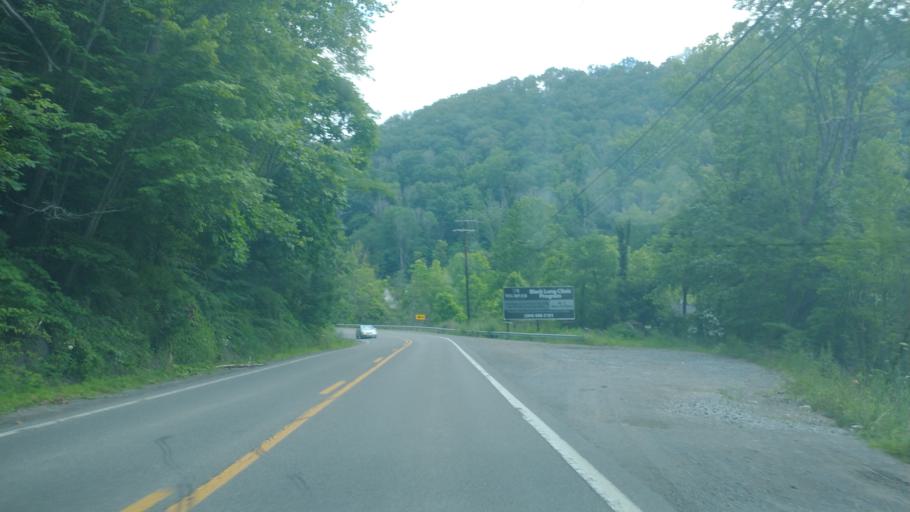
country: US
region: West Virginia
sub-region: McDowell County
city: Welch
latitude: 37.4018
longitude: -81.4194
